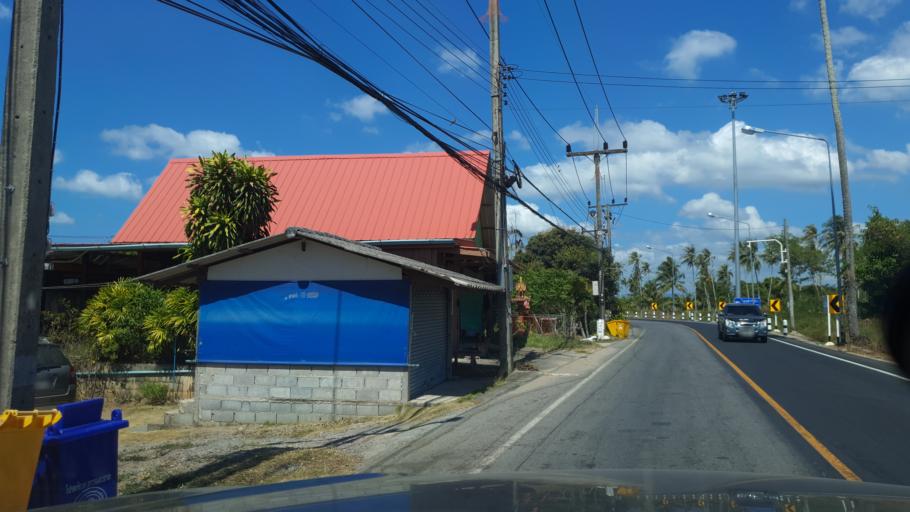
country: TH
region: Phuket
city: Thalang
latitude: 8.1420
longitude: 98.3065
